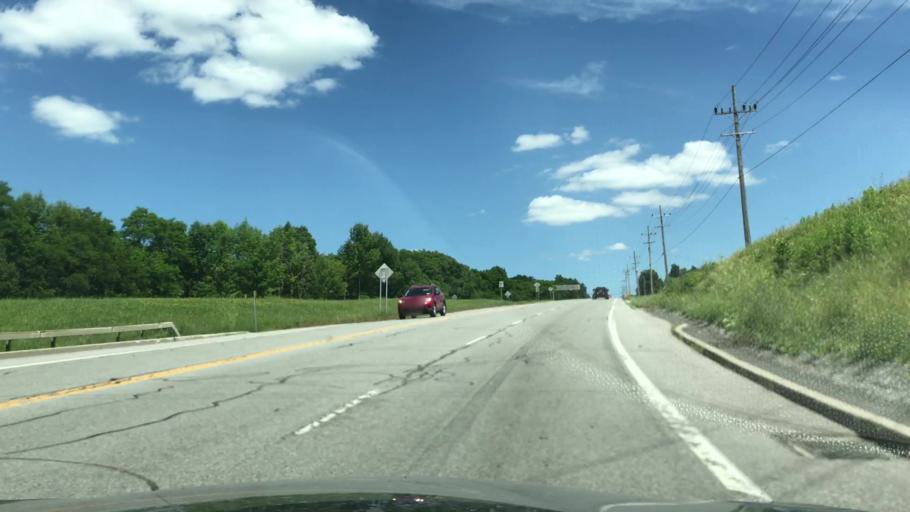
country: US
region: New York
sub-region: Wyoming County
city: Warsaw
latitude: 42.7466
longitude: -78.1242
